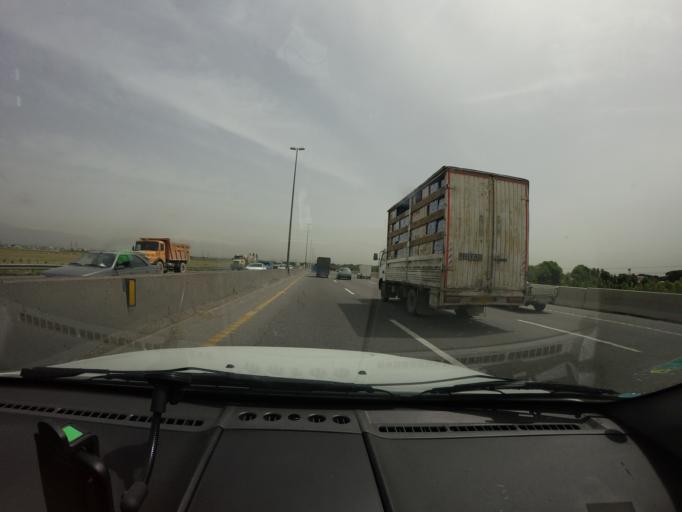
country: IR
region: Tehran
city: Eslamshahr
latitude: 35.6035
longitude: 51.1927
